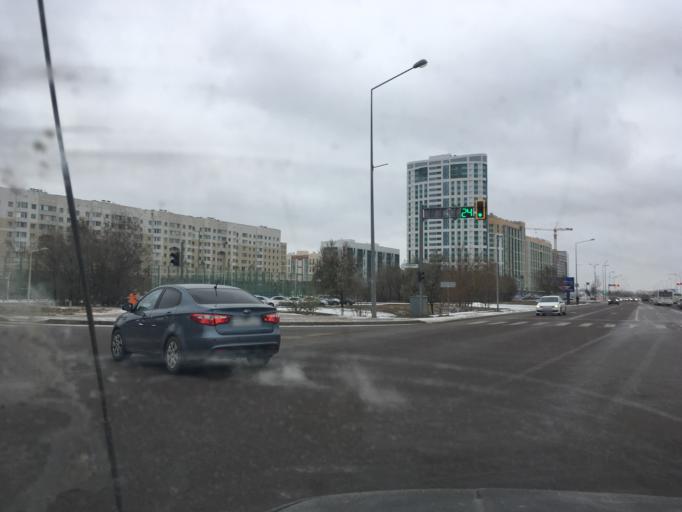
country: KZ
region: Astana Qalasy
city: Astana
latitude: 51.1185
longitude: 71.4118
